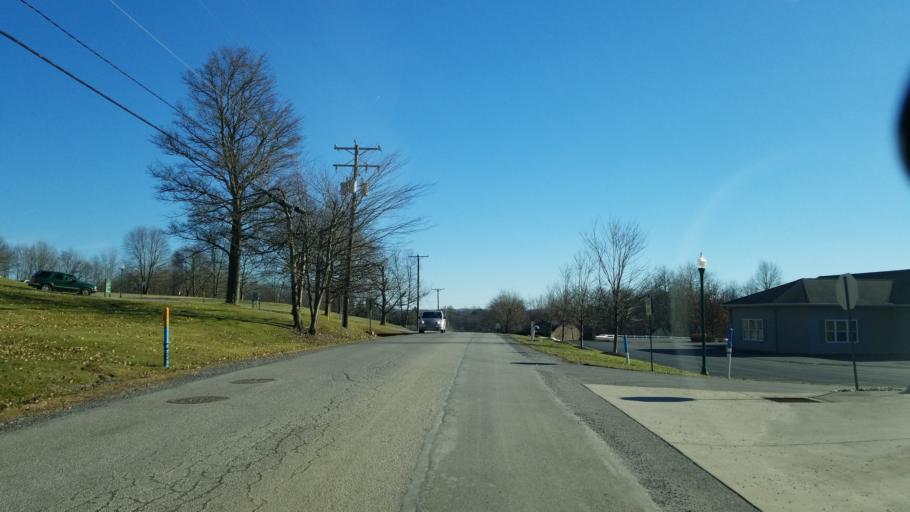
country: US
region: Pennsylvania
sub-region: Clearfield County
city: Sandy
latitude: 41.1270
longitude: -78.7855
